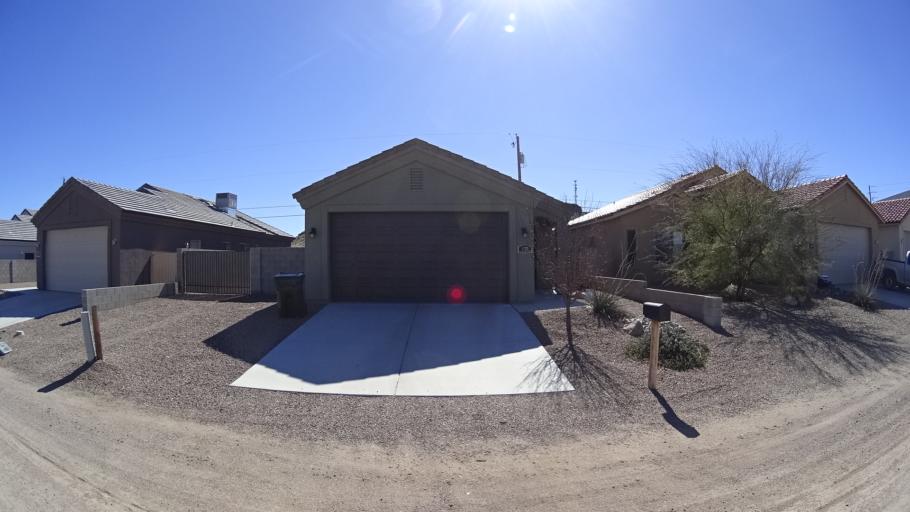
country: US
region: Arizona
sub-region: Mohave County
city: Kingman
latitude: 35.2039
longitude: -114.0393
